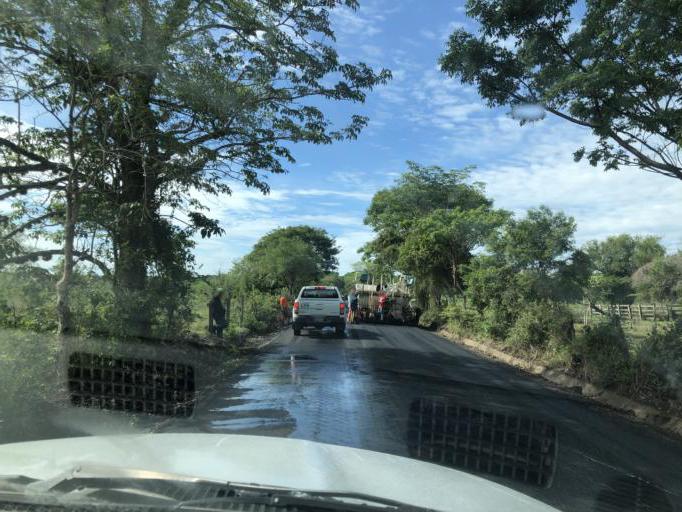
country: MX
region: Veracruz
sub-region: Alto Lucero de Gutierrez Barrios
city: Palma Sola
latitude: 19.8083
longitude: -96.5439
